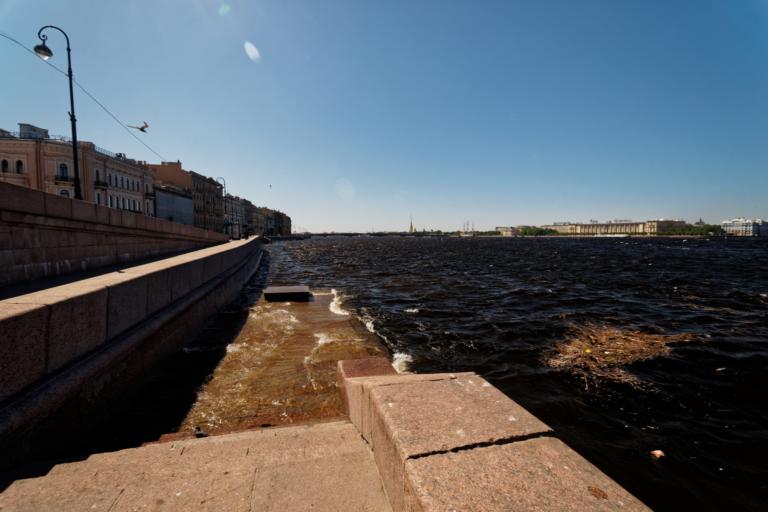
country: RU
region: St.-Petersburg
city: Centralniy
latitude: 59.9500
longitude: 30.3478
